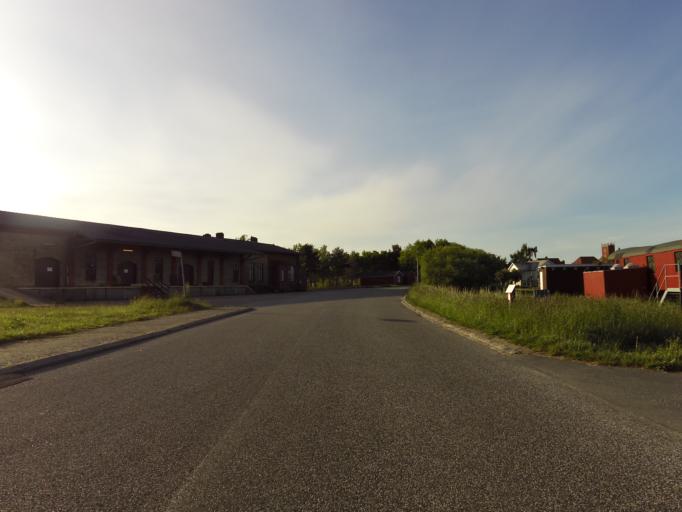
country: DK
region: South Denmark
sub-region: Tonder Kommune
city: Tonder
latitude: 54.9308
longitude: 8.8606
